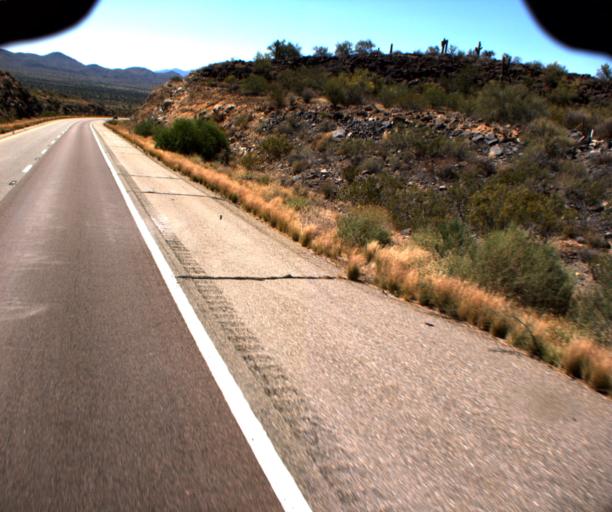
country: US
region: Arizona
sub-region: Yavapai County
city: Bagdad
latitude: 34.5019
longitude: -113.4016
